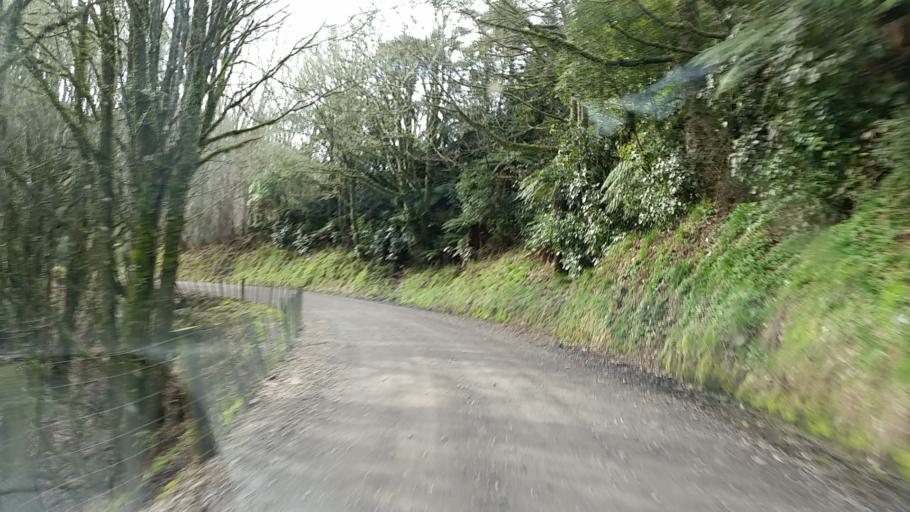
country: NZ
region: Taranaki
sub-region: New Plymouth District
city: Waitara
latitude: -39.1626
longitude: 174.5744
